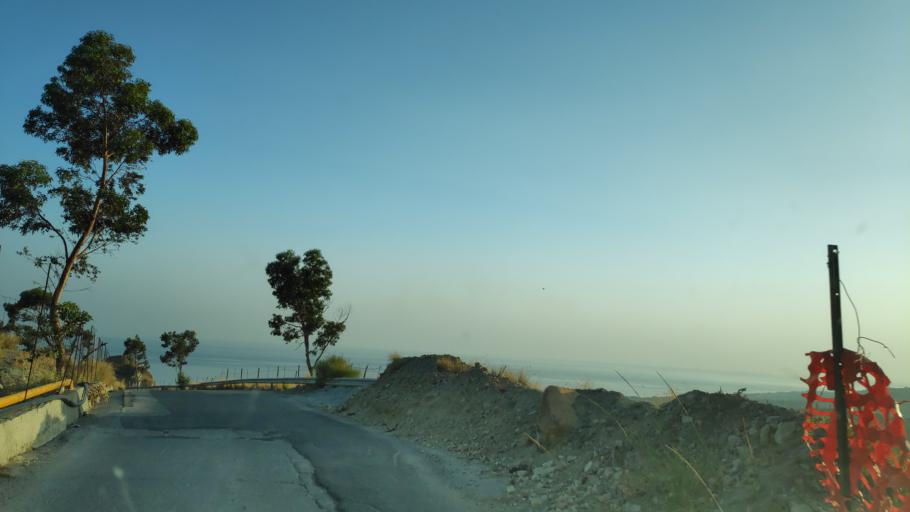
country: IT
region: Calabria
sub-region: Provincia di Reggio Calabria
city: Bova Marina
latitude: 37.9541
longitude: 15.9209
